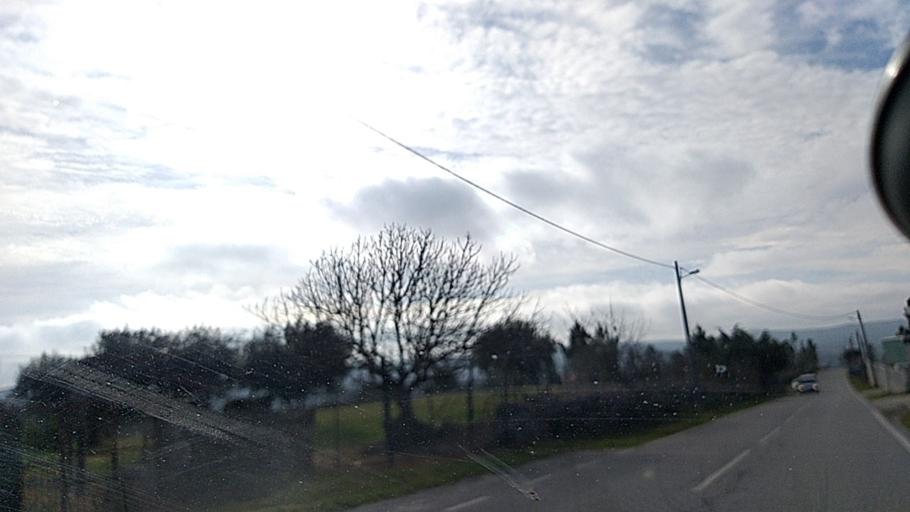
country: PT
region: Guarda
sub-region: Aguiar da Beira
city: Aguiar da Beira
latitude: 40.7432
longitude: -7.5551
